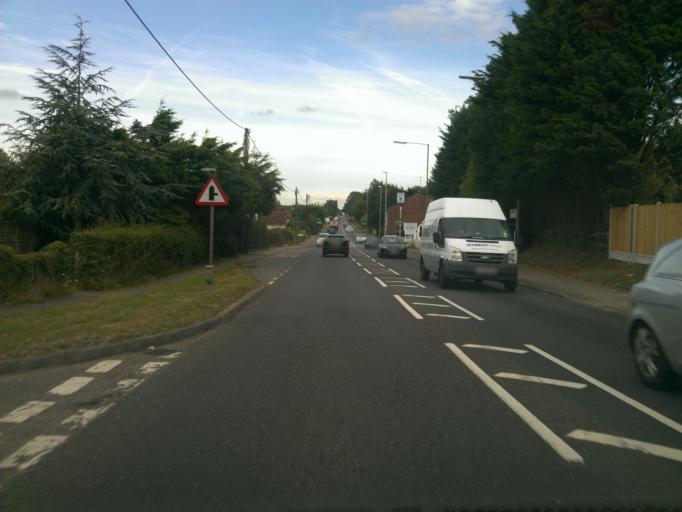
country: GB
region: England
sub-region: Essex
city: Rayne
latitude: 51.8778
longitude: 0.6213
